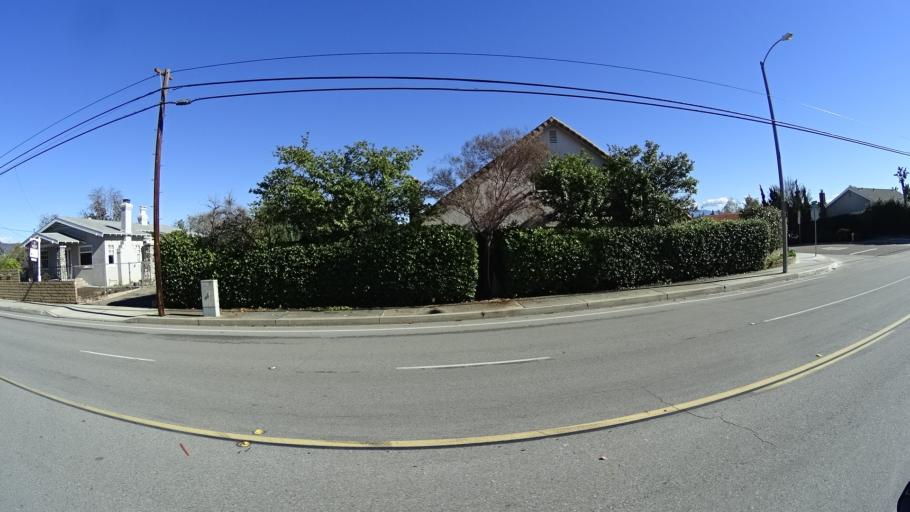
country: US
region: California
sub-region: Orange County
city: Placentia
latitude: 33.8947
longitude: -117.8550
